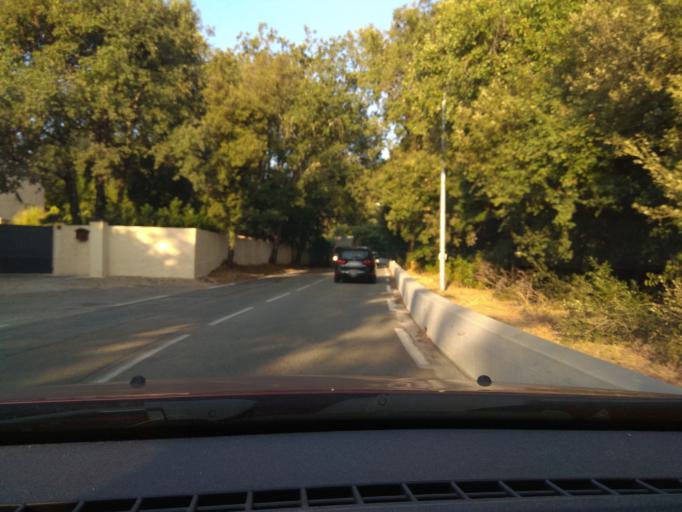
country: FR
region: Provence-Alpes-Cote d'Azur
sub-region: Departement des Alpes-Maritimes
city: Le Rouret
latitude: 43.6509
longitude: 7.0268
